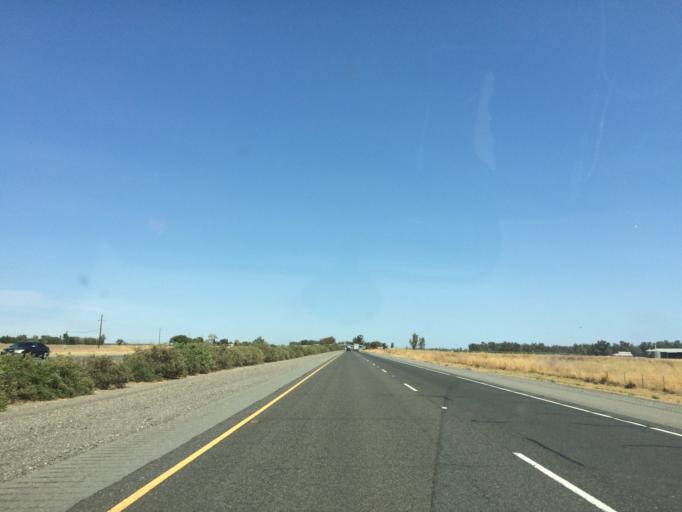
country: US
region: California
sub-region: Glenn County
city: Willows
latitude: 39.5731
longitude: -122.2117
